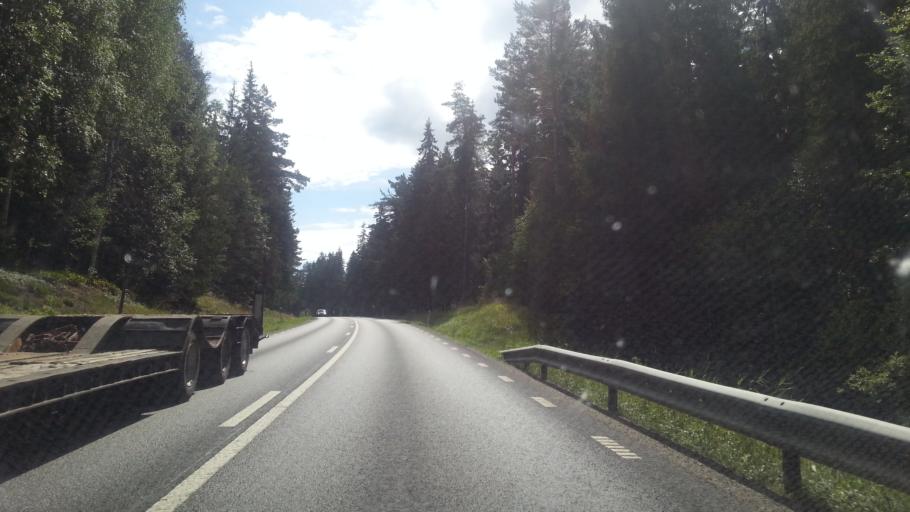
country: SE
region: OErebro
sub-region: Lindesbergs Kommun
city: Stora
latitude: 59.6555
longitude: 15.1072
